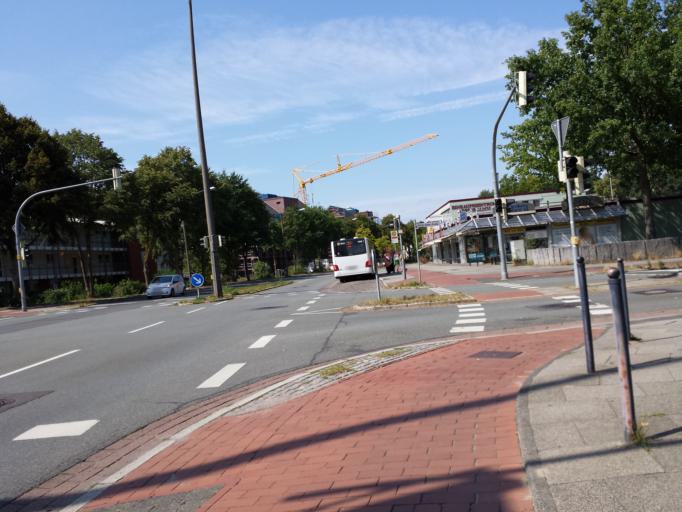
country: DE
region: Bremen
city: Bremen
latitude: 53.0354
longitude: 8.8416
